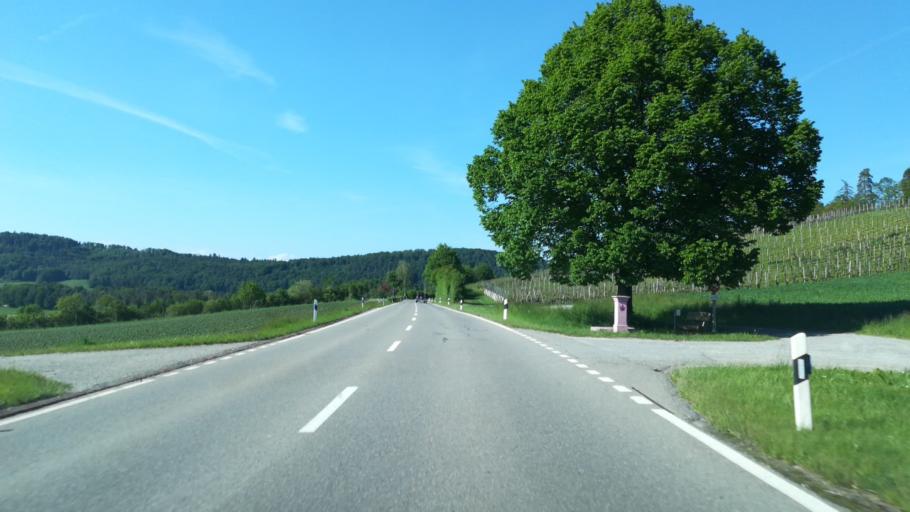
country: CH
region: Thurgau
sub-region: Frauenfeld District
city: Diessenhofen
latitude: 47.6506
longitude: 8.7890
